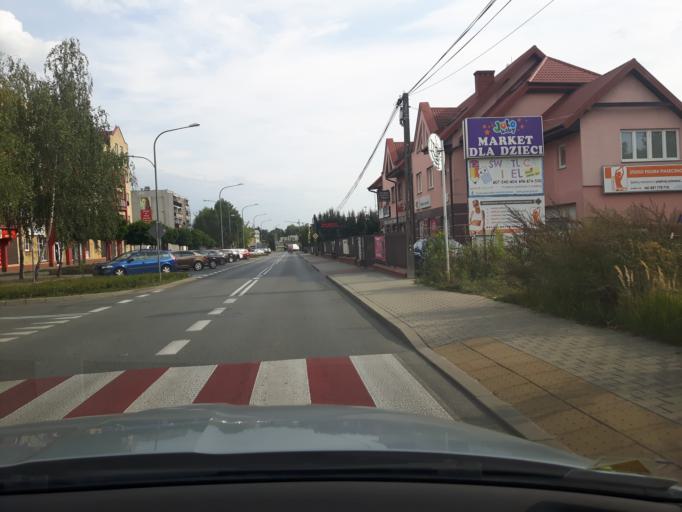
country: PL
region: Masovian Voivodeship
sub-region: Powiat piaseczynski
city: Piaseczno
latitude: 52.0770
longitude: 21.0163
